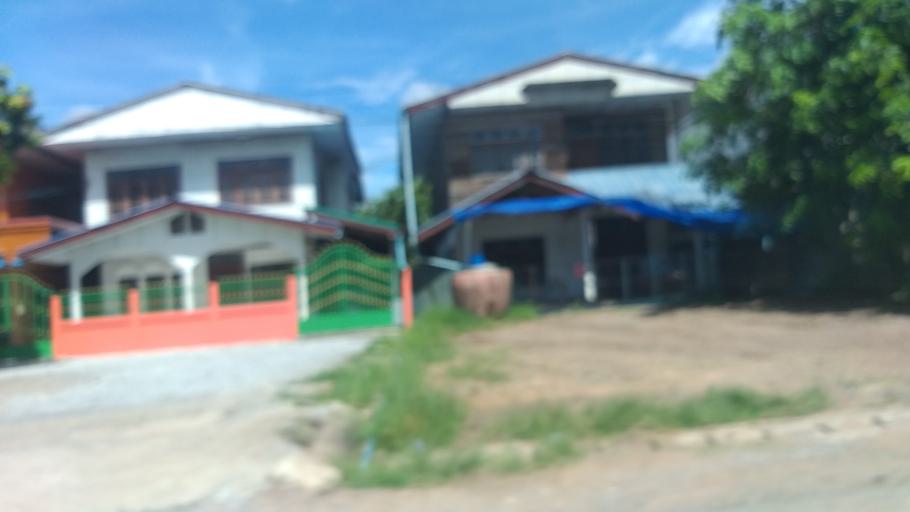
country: TH
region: Khon Kaen
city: Nong Ruea
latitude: 16.4540
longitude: 102.4412
